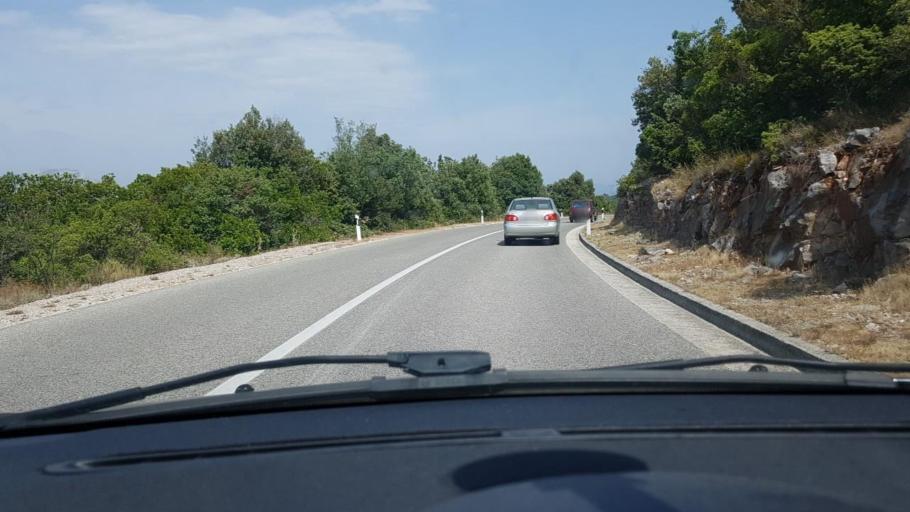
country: HR
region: Dubrovacko-Neretvanska
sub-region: Grad Korcula
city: Zrnovo
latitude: 42.9408
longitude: 17.0573
